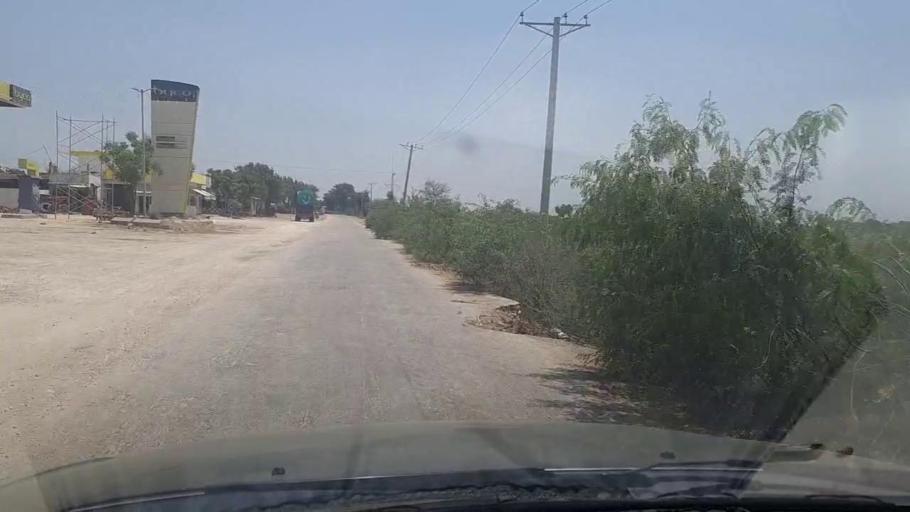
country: PK
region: Sindh
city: Chambar
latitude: 25.2642
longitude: 68.6479
